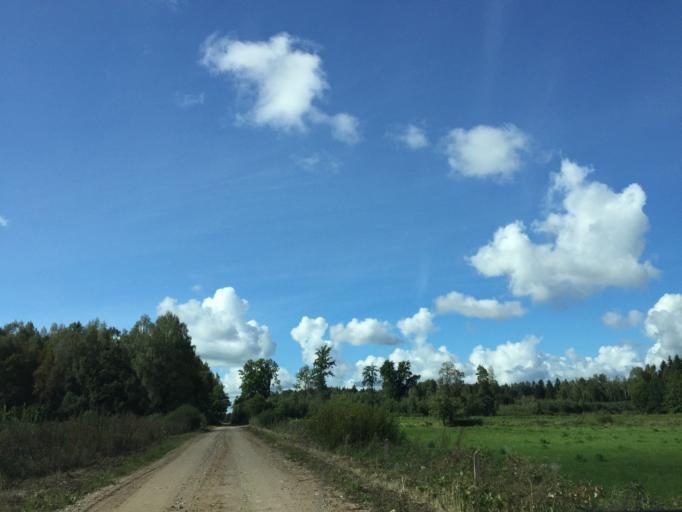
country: LV
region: Kuldigas Rajons
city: Kuldiga
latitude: 56.9917
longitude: 21.8423
